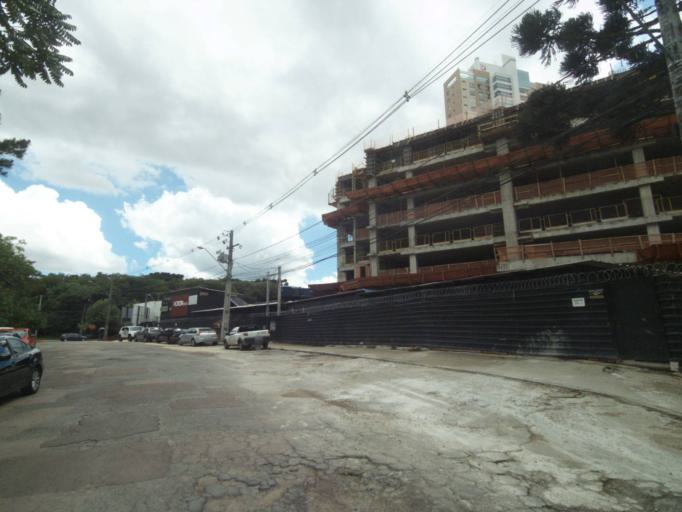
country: BR
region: Parana
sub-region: Curitiba
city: Curitiba
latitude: -25.4404
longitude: -49.3434
